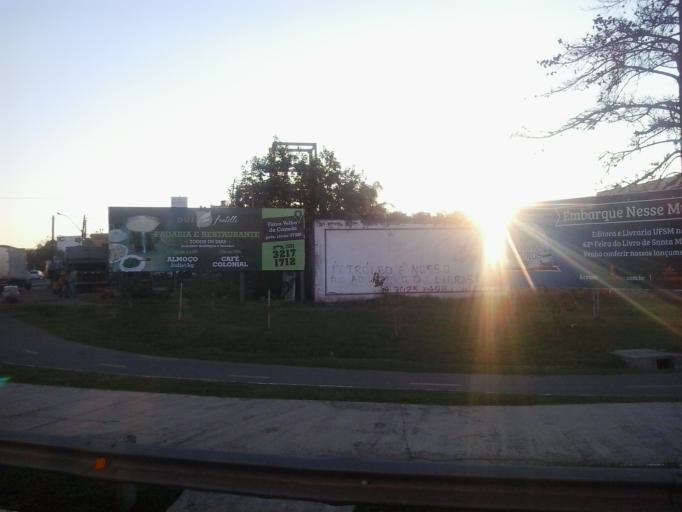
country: BR
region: Rio Grande do Sul
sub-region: Santa Maria
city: Santa Maria
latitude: -29.7051
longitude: -53.7160
